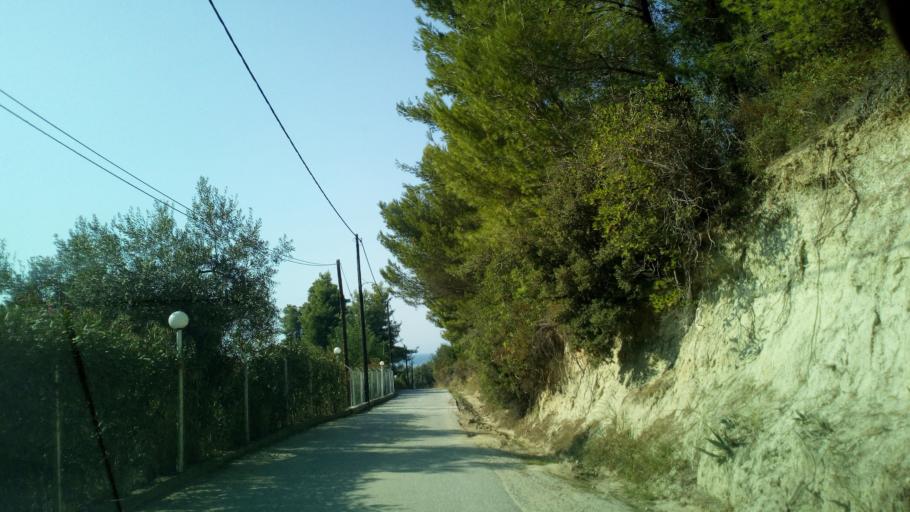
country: GR
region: Central Macedonia
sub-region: Nomos Chalkidikis
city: Pefkochori
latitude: 39.9721
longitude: 23.6537
